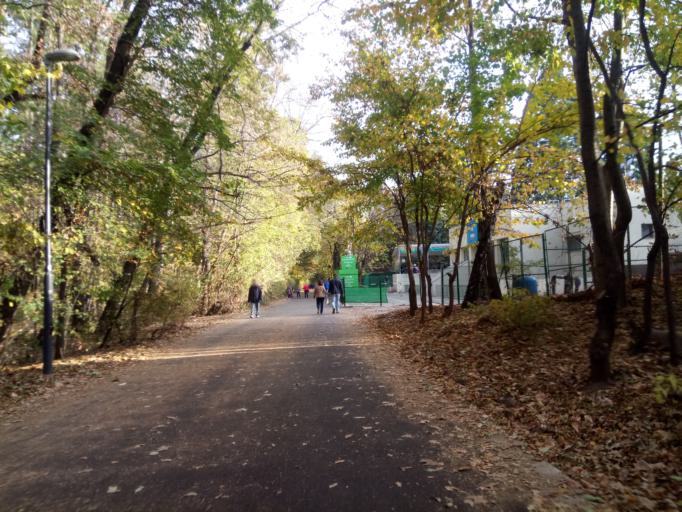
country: BG
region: Sofia-Capital
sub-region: Stolichna Obshtina
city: Sofia
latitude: 42.6777
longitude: 23.3463
